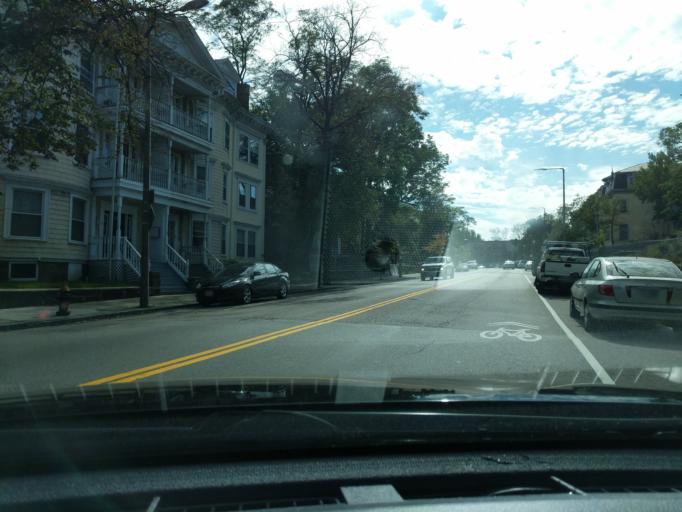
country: US
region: Massachusetts
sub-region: Suffolk County
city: Jamaica Plain
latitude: 42.3153
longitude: -71.0833
